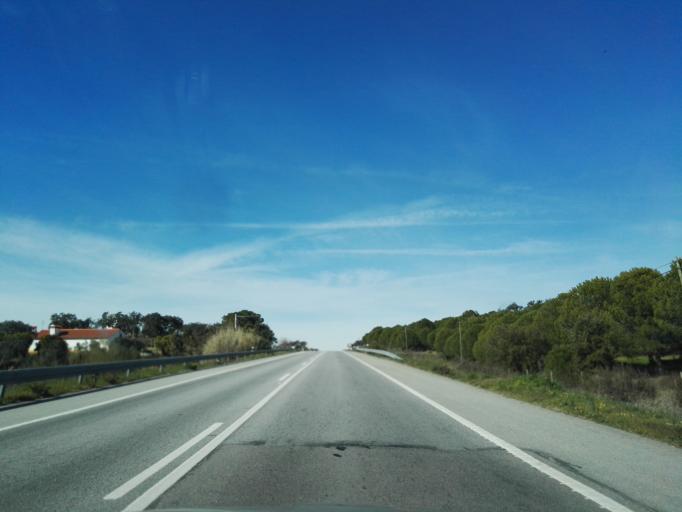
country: PT
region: Portalegre
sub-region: Arronches
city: Arronches
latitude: 39.1470
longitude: -7.3061
